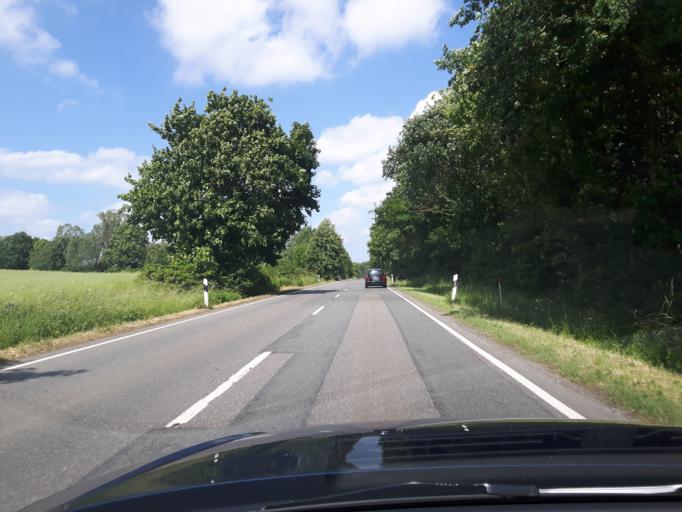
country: DE
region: Schleswig-Holstein
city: Sierksdorf
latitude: 54.0656
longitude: 10.7614
